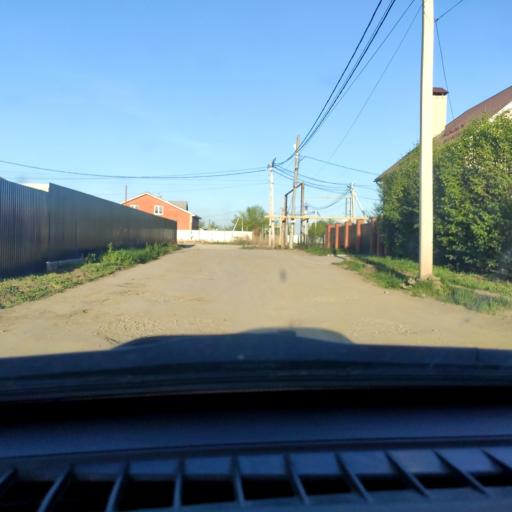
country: RU
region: Samara
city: Tol'yatti
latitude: 53.5634
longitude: 49.4061
